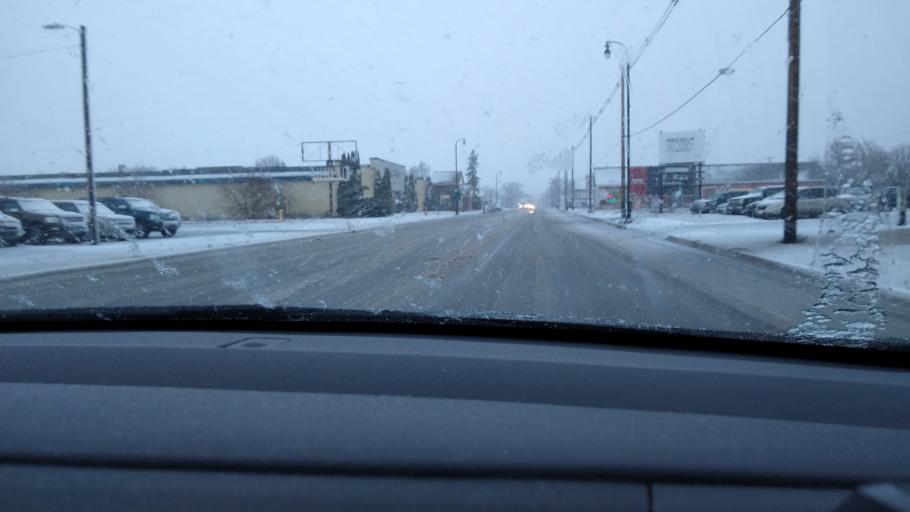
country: US
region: Michigan
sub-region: Delta County
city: Escanaba
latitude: 45.7496
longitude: -87.0719
